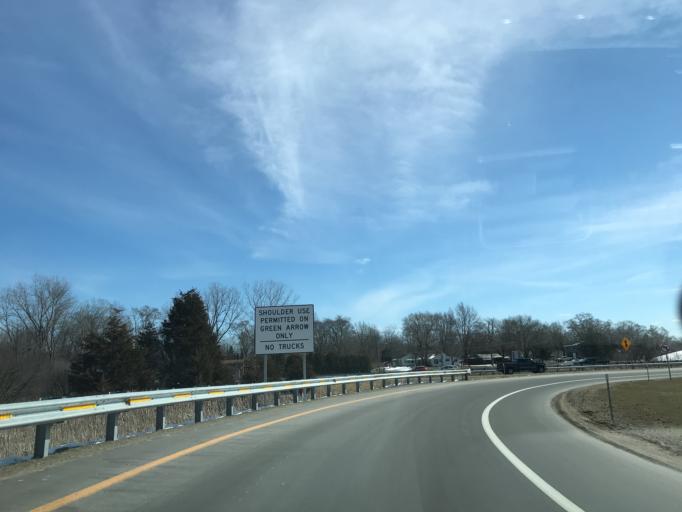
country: US
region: Michigan
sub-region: Livingston County
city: Whitmore Lake
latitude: 42.3961
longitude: -83.7648
